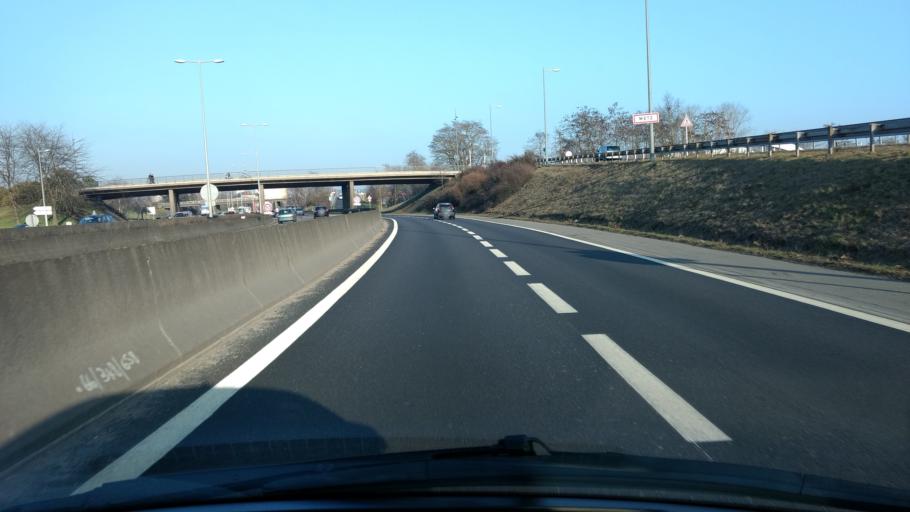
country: FR
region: Lorraine
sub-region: Departement de la Moselle
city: Metz
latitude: 49.1303
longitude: 6.1671
